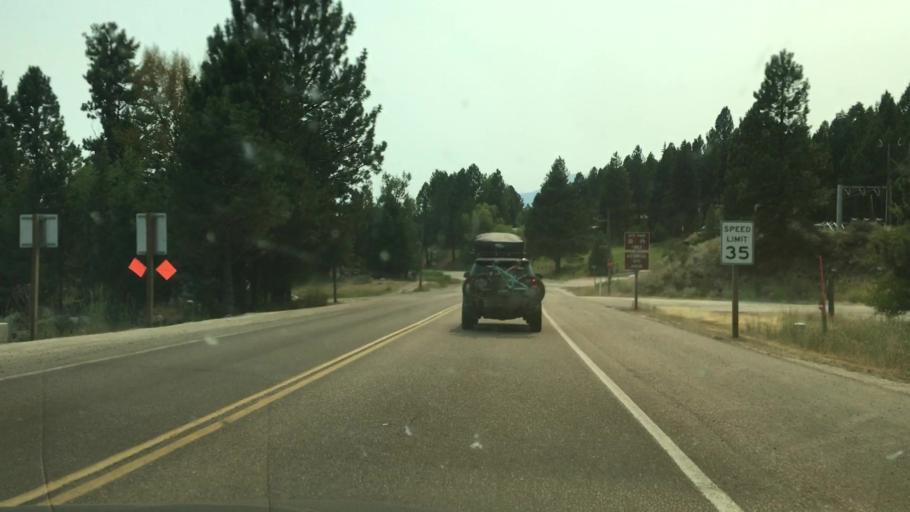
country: US
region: Idaho
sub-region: Valley County
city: Cascade
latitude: 44.5238
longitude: -116.0449
